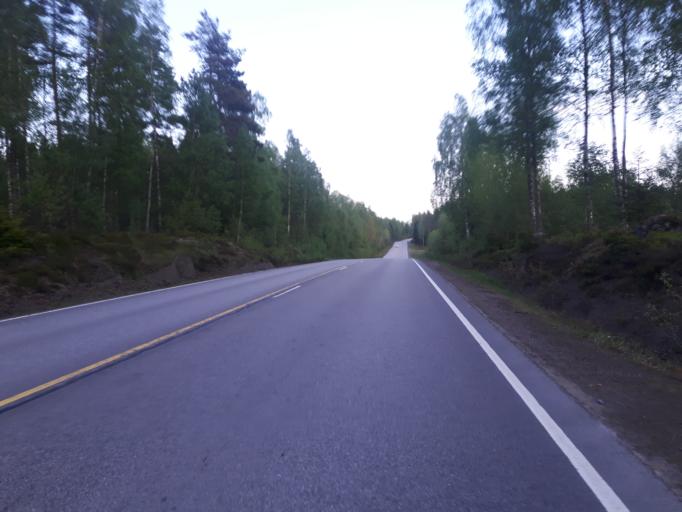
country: FI
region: Uusimaa
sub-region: Loviisa
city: Perna
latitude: 60.4592
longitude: 26.0711
